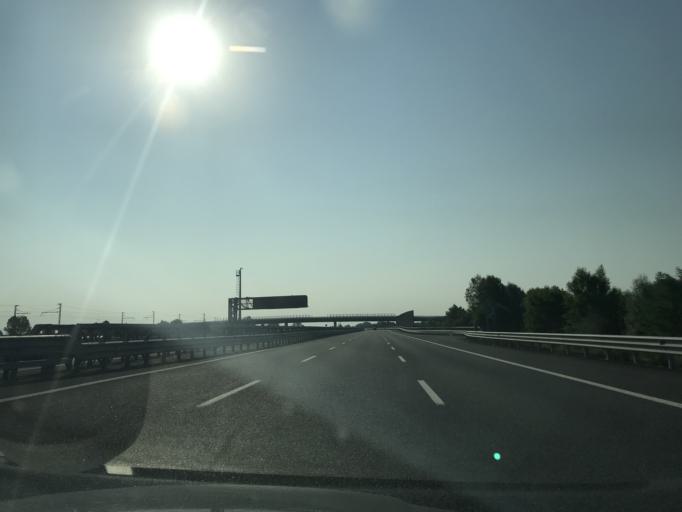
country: IT
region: Lombardy
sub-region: Provincia di Bergamo
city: Casirate d'Adda
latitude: 45.5049
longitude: 9.5737
